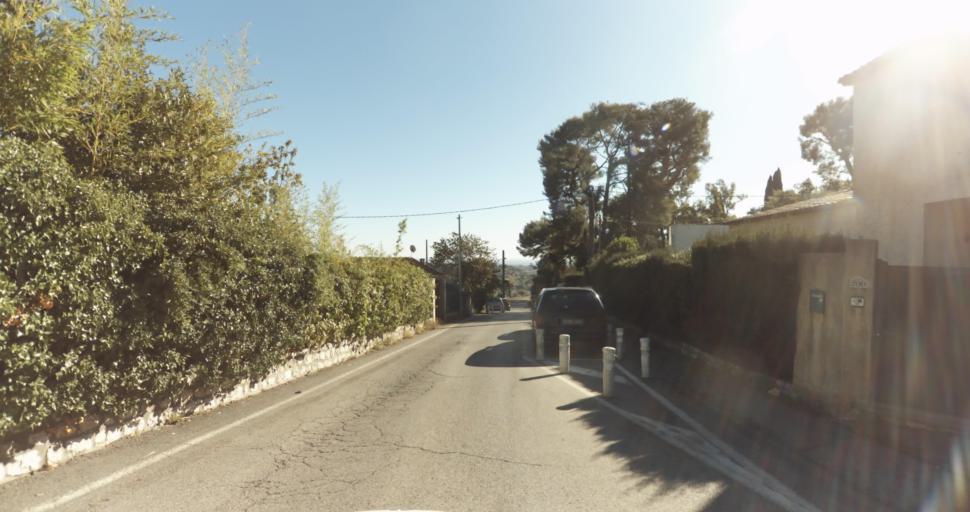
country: FR
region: Provence-Alpes-Cote d'Azur
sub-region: Departement des Alpes-Maritimes
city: Vence
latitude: 43.7163
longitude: 7.1201
